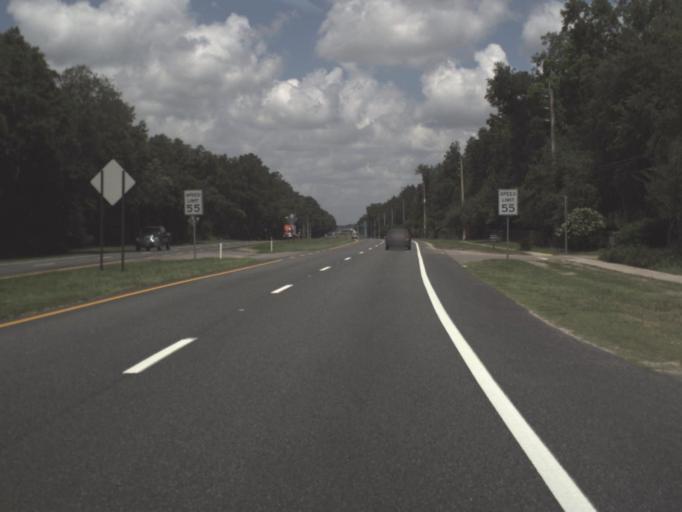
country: US
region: Florida
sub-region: Saint Johns County
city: Fruit Cove
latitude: 30.1456
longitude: -81.5201
